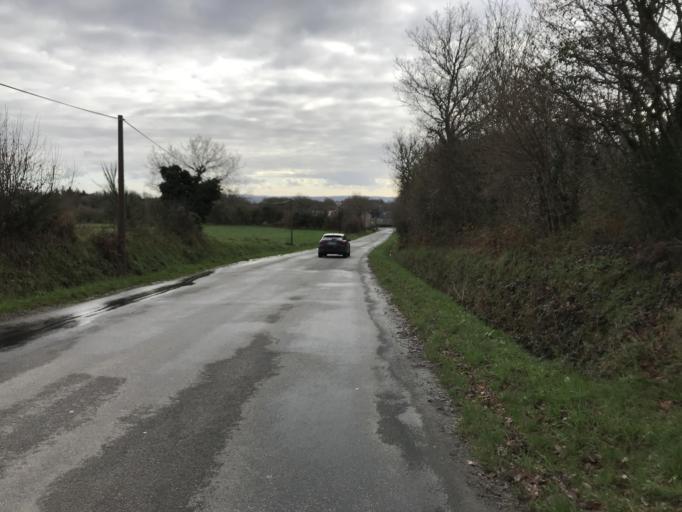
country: FR
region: Brittany
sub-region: Departement du Finistere
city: Plougastel-Daoulas
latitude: 48.3751
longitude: -4.3504
